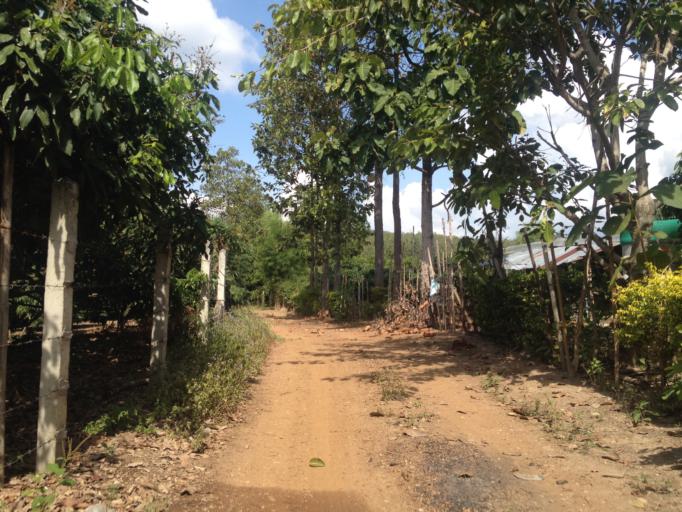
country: TH
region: Chiang Mai
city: Hang Dong
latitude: 18.7013
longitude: 98.8879
